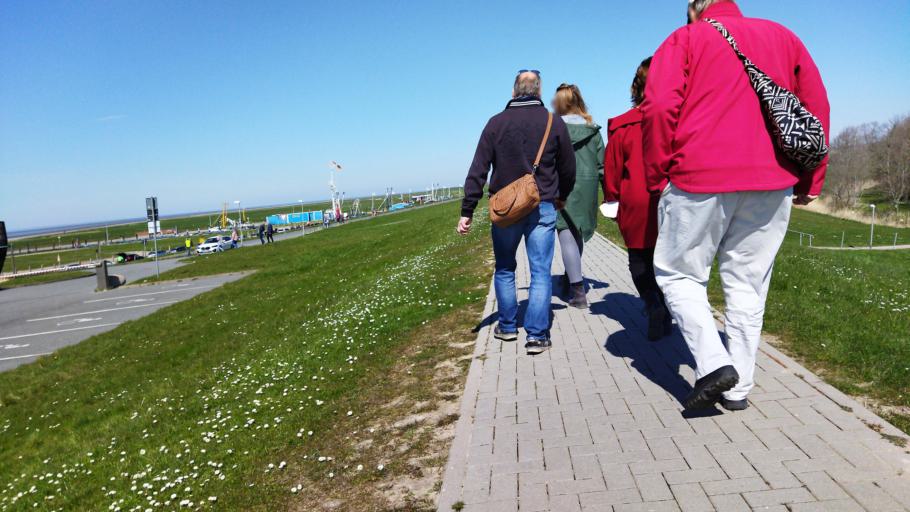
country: DE
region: Lower Saxony
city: Wremen
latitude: 53.6459
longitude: 8.4957
